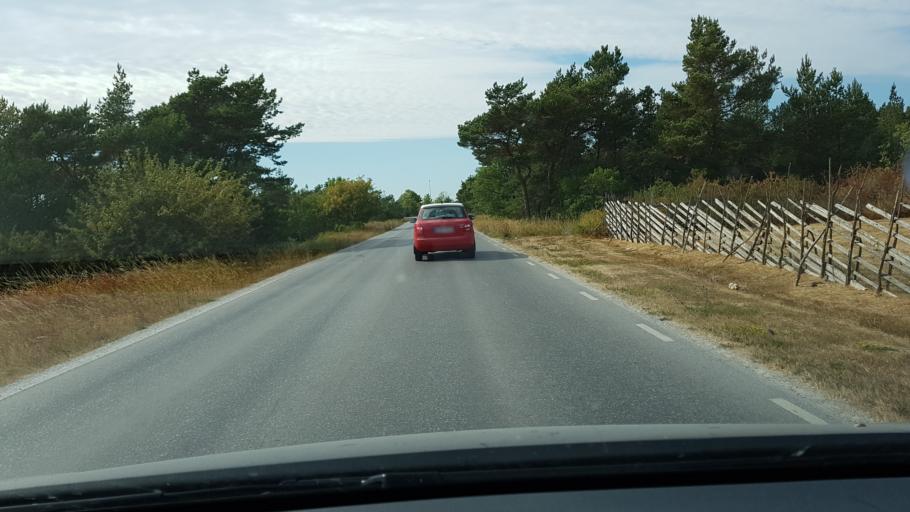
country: SE
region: Gotland
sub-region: Gotland
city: Visby
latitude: 57.6507
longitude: 18.3206
